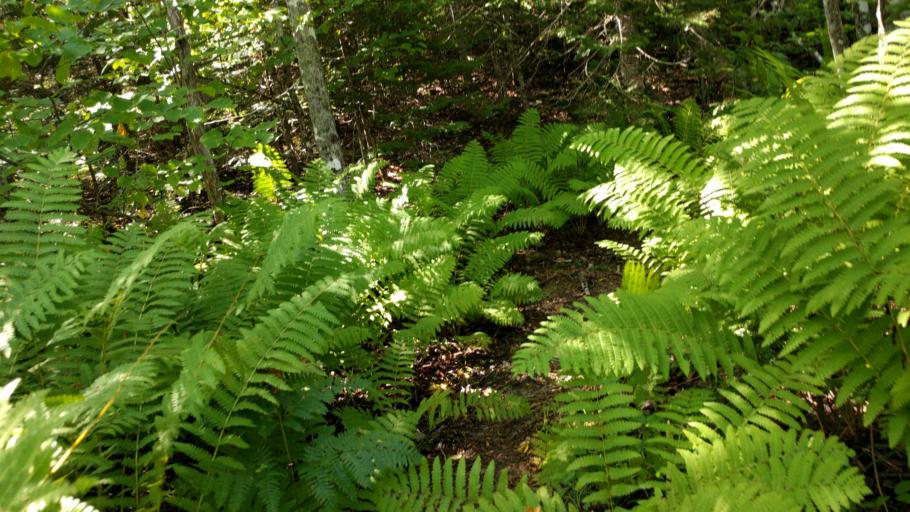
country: US
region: Maine
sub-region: Penobscot County
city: Patten
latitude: 46.0863
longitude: -68.7750
